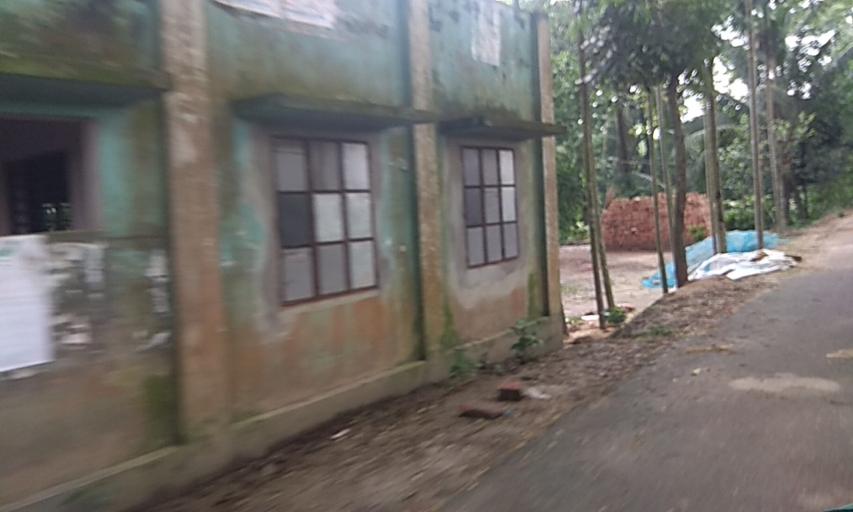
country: BD
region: Dhaka
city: Dohar
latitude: 23.4741
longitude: 90.0382
